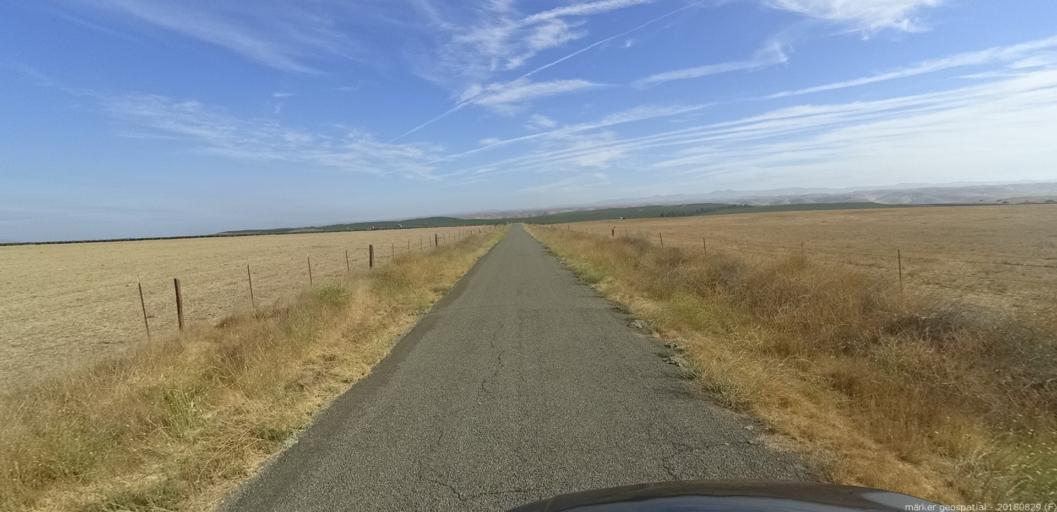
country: US
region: California
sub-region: Monterey County
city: King City
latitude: 36.0536
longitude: -120.9792
